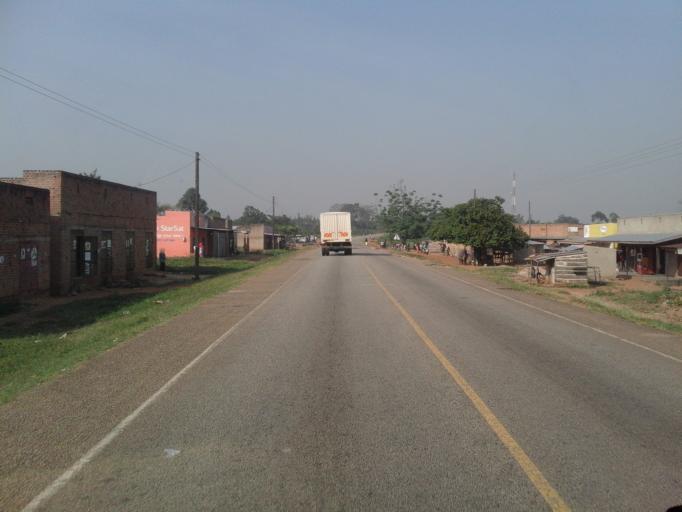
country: UG
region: Eastern Region
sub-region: Budaka District
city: Budaka
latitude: 1.0408
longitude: 34.0245
